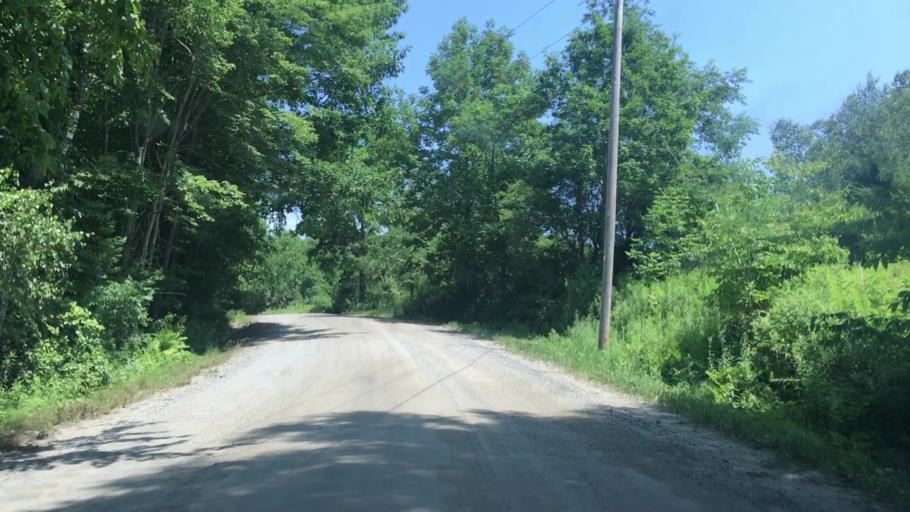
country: US
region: Maine
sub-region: Kennebec County
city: Monmouth
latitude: 44.2870
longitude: -70.0553
